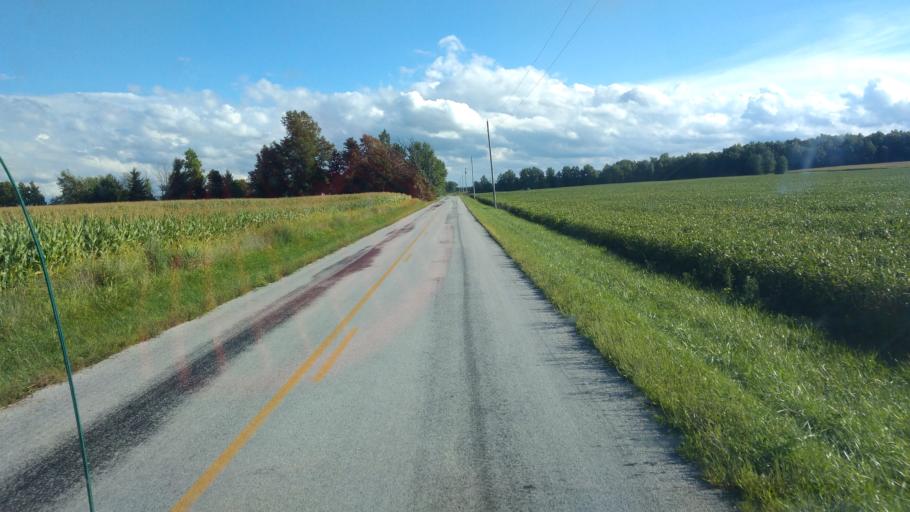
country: US
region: Ohio
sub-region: Hardin County
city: Forest
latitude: 40.7596
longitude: -83.6048
